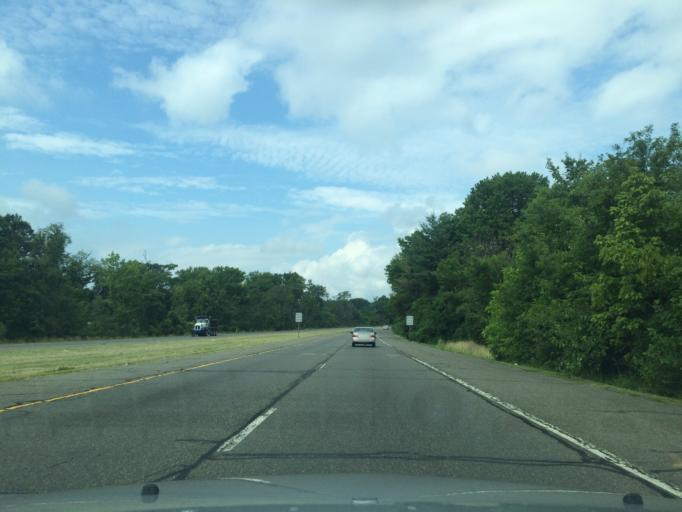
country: US
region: Maryland
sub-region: Prince George's County
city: Coral Hills
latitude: 38.8636
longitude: -76.9390
